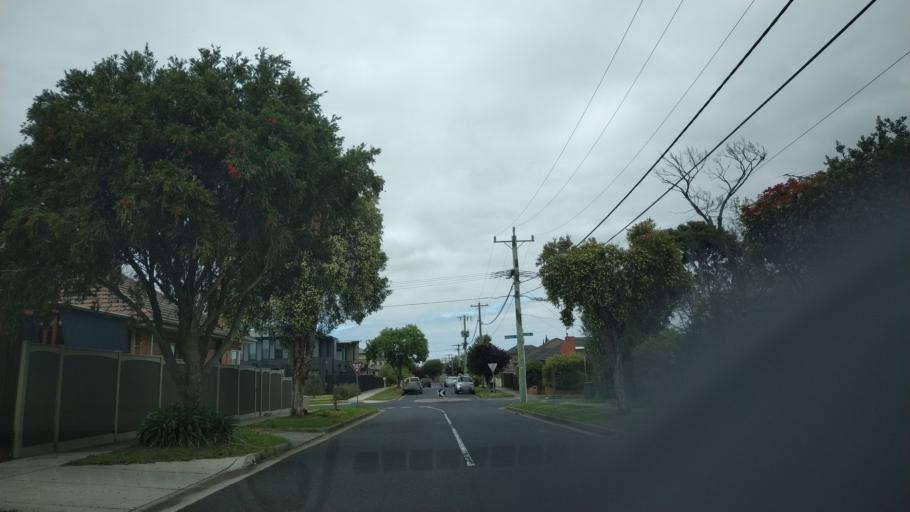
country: AU
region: Victoria
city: Hughesdale
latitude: -37.9096
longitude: 145.0816
